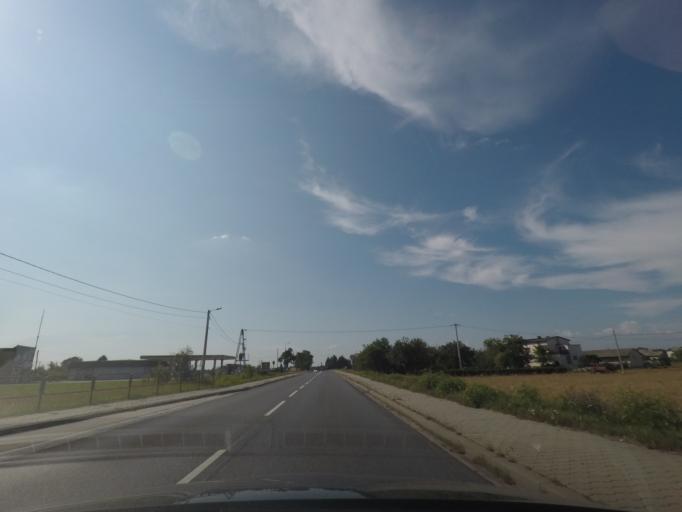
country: PL
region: Silesian Voivodeship
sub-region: Powiat pszczynski
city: Radostowice
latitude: 50.0068
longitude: 18.8694
